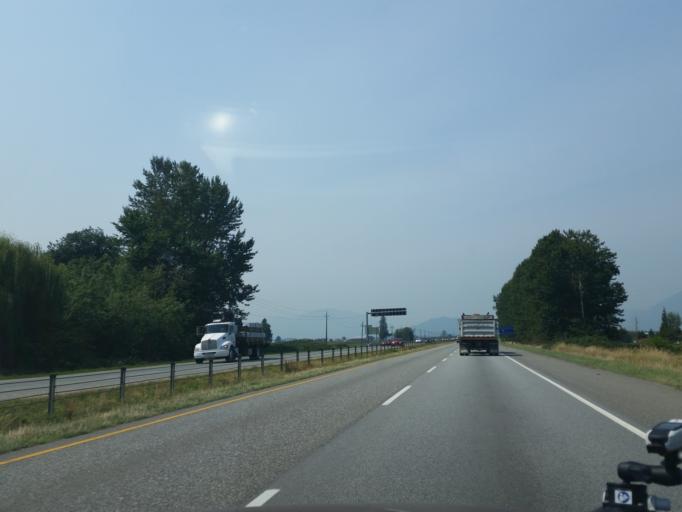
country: CA
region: British Columbia
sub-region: Fraser Valley Regional District
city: Chilliwack
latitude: 49.1549
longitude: -121.8504
